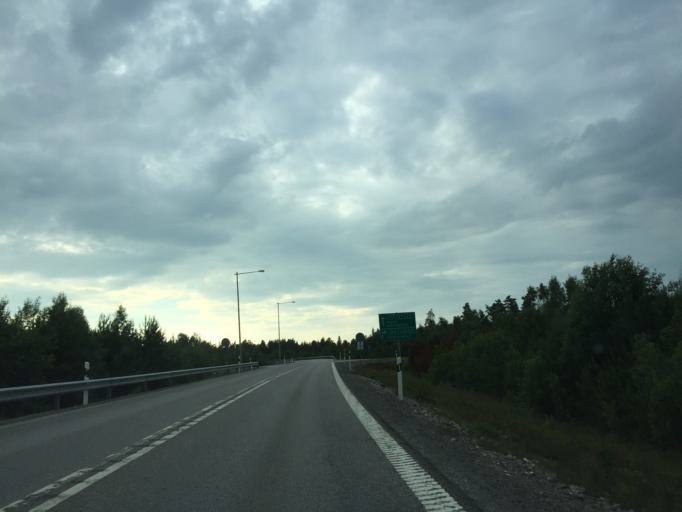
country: SE
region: OErebro
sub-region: Lindesbergs Kommun
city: Fellingsbro
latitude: 59.3388
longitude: 15.5453
